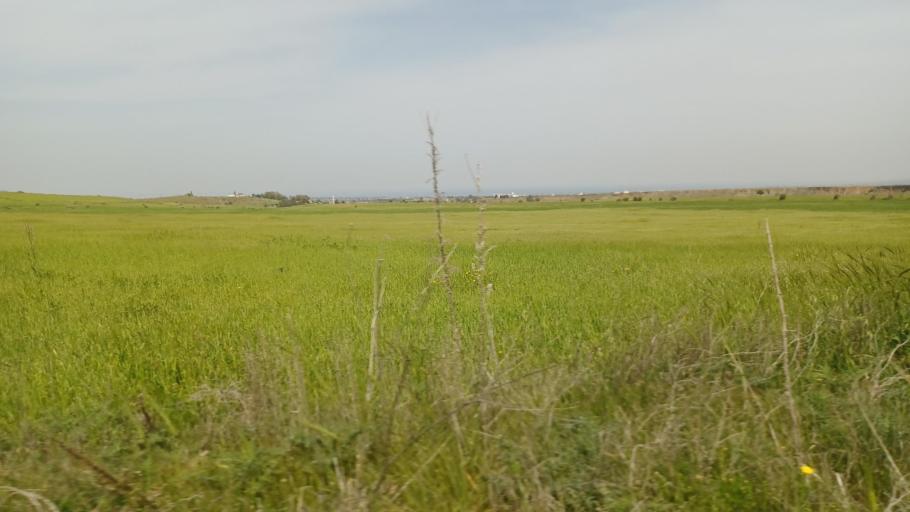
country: CY
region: Lefkosia
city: Astromeritis
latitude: 35.1082
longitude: 32.9634
